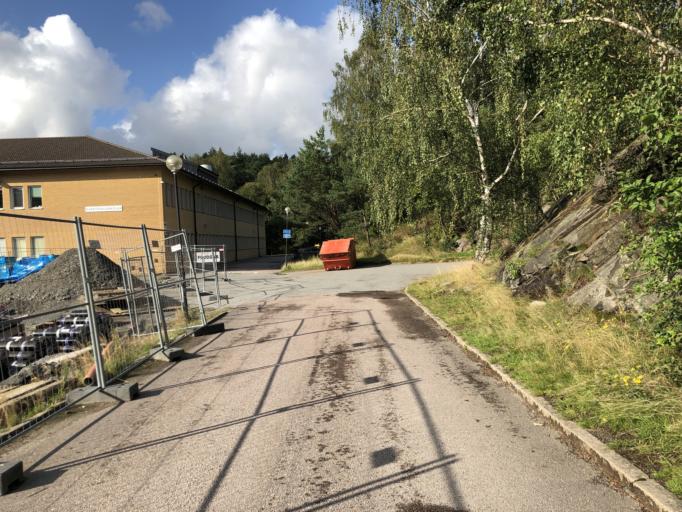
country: SE
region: Vaestra Goetaland
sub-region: Goteborg
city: Majorna
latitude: 57.7320
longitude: 11.9013
